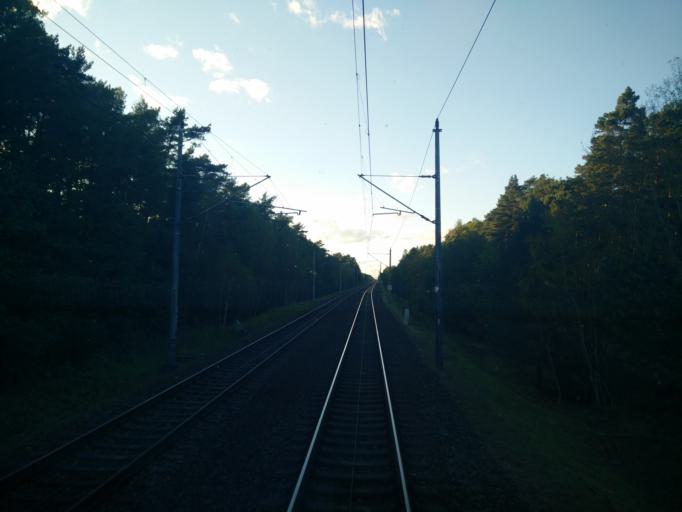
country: DE
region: Brandenburg
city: Plattenburg
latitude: 52.9112
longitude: 12.0630
